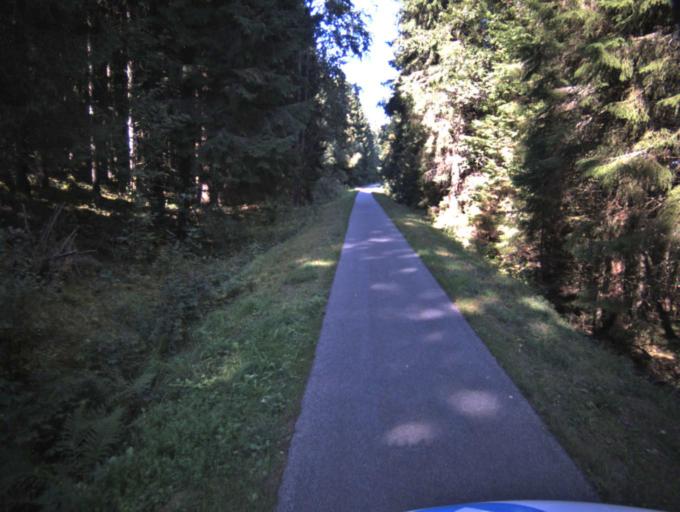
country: SE
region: Vaestra Goetaland
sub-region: Ulricehamns Kommun
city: Ulricehamn
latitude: 57.8209
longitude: 13.3470
